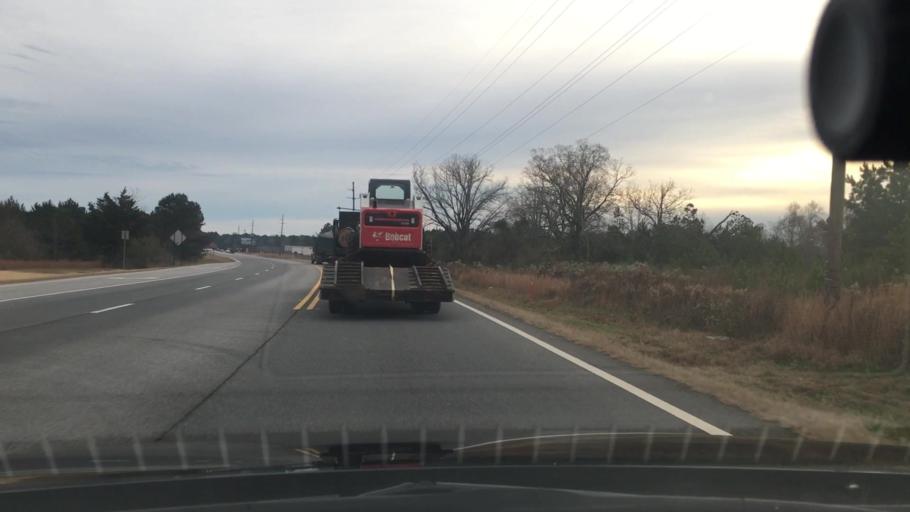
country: US
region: Georgia
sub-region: Coweta County
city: Senoia
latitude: 33.2933
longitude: -84.5793
